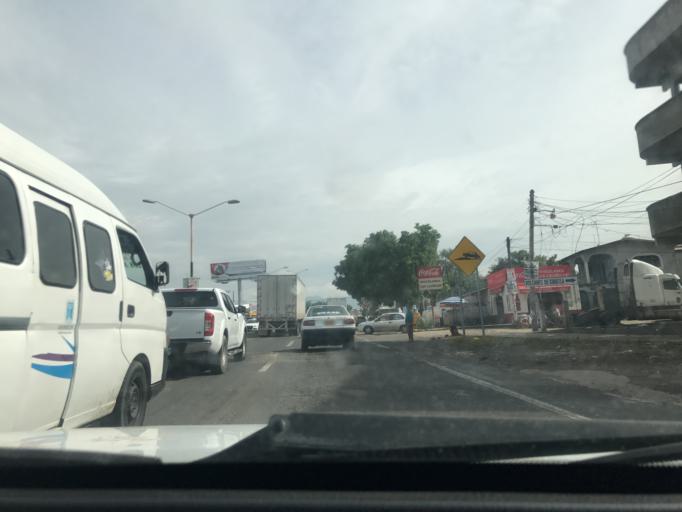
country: MX
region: Morelos
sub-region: Cuautla
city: Tierra Larga (Campo Nuevo)
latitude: 18.8574
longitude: -98.9351
